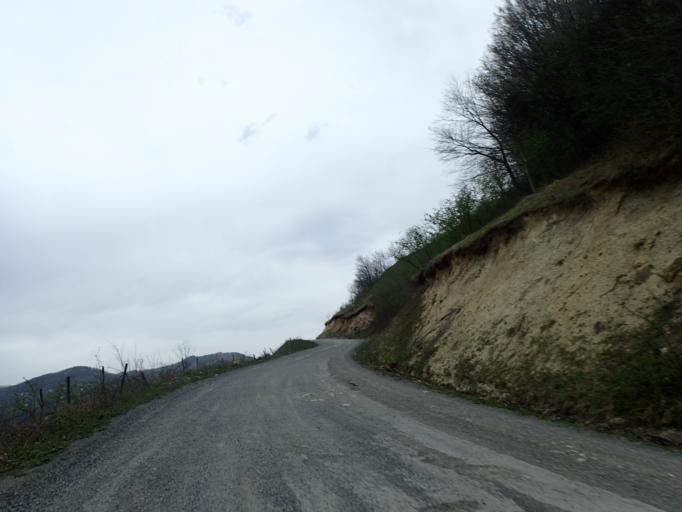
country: TR
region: Ordu
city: Korgan
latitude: 40.7648
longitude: 37.3374
